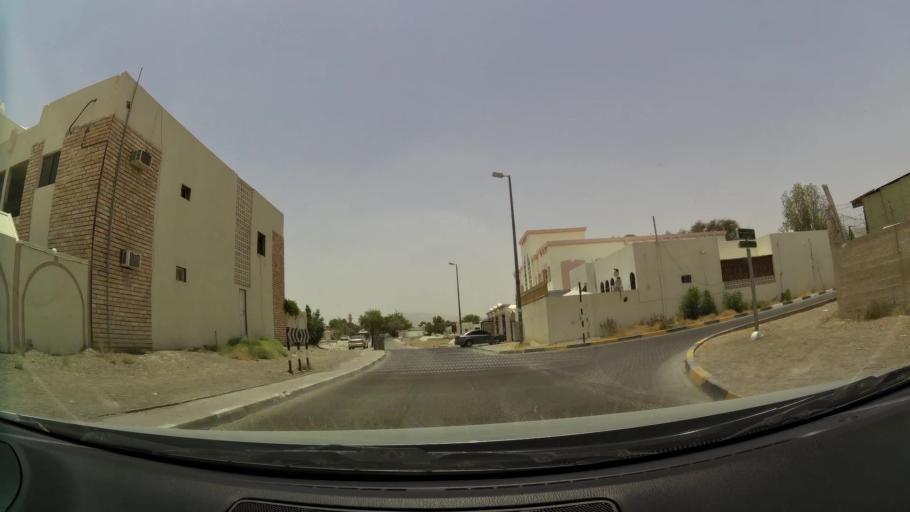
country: AE
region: Abu Dhabi
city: Al Ain
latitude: 24.2100
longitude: 55.7545
